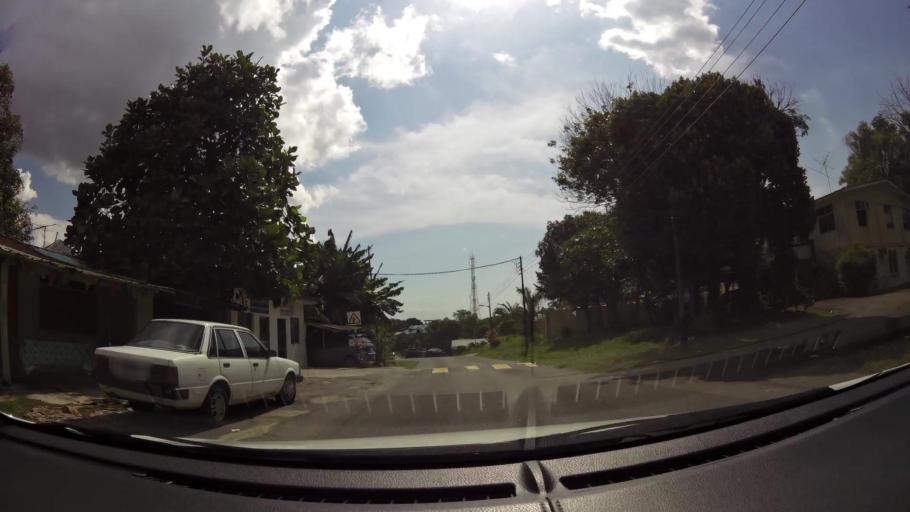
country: BN
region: Brunei and Muara
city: Bandar Seri Begawan
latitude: 4.9572
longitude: 114.9579
